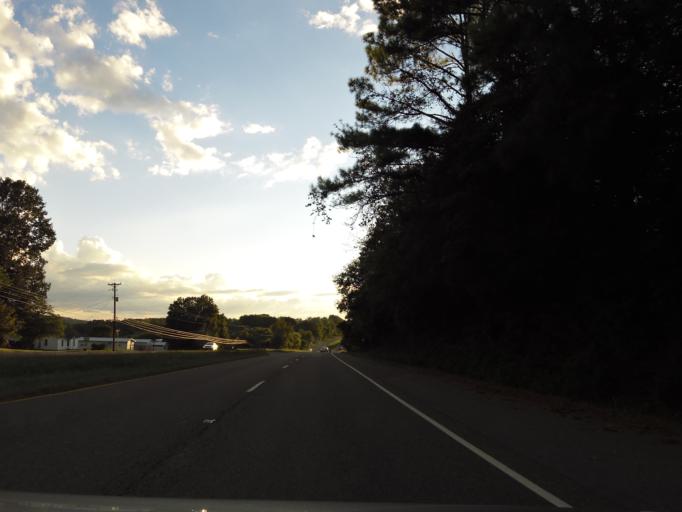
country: US
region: Tennessee
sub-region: Jefferson County
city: New Market
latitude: 36.0706
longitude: -83.6426
